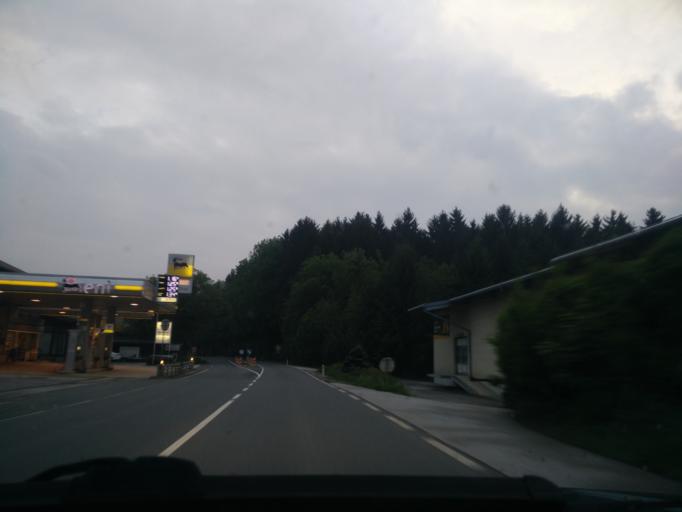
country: AT
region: Salzburg
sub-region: Politischer Bezirk Salzburg-Umgebung
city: Elixhausen
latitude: 47.8601
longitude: 13.0591
